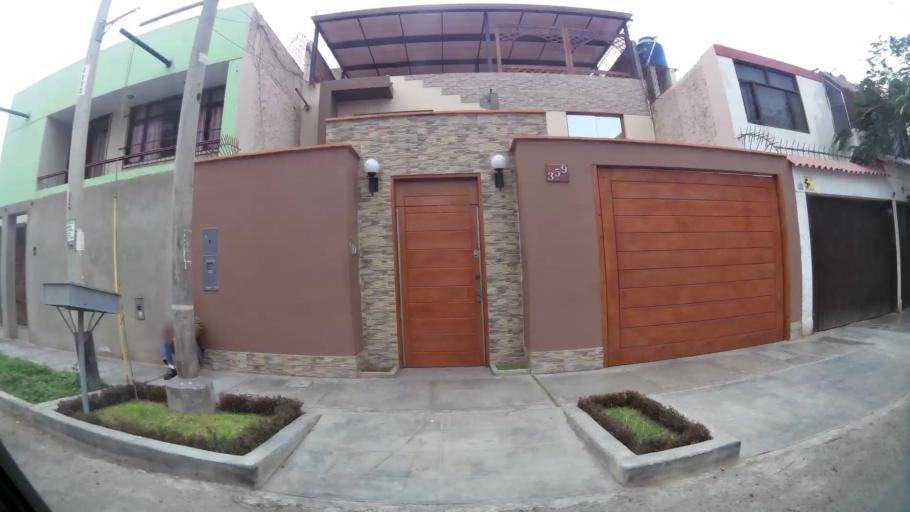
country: PE
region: La Libertad
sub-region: Provincia de Trujillo
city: Buenos Aires
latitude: -8.1332
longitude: -79.0422
